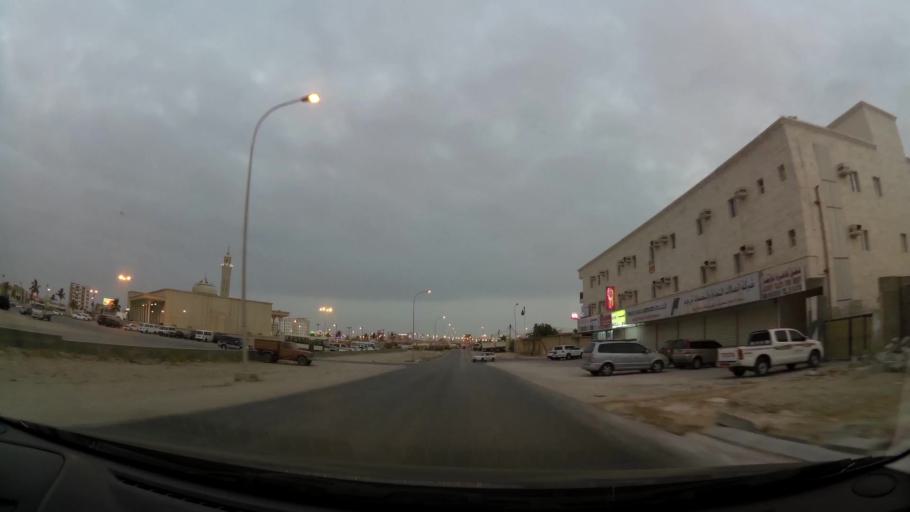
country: OM
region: Zufar
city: Salalah
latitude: 17.0234
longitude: 54.0554
